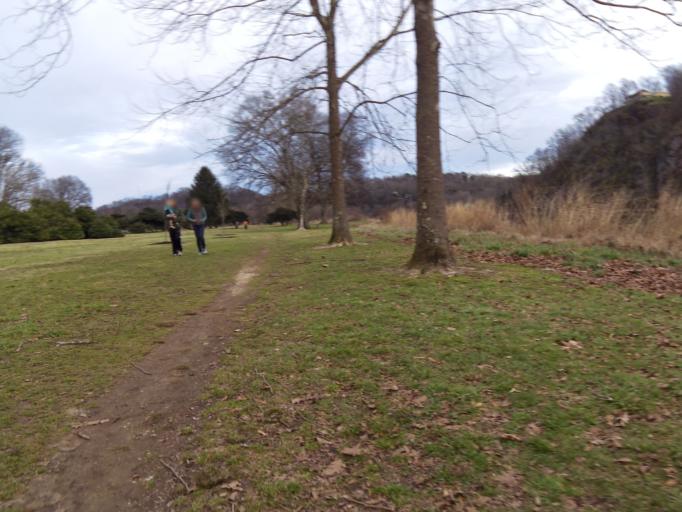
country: US
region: Tennessee
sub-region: Knox County
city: Knoxville
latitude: 35.9266
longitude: -83.9620
